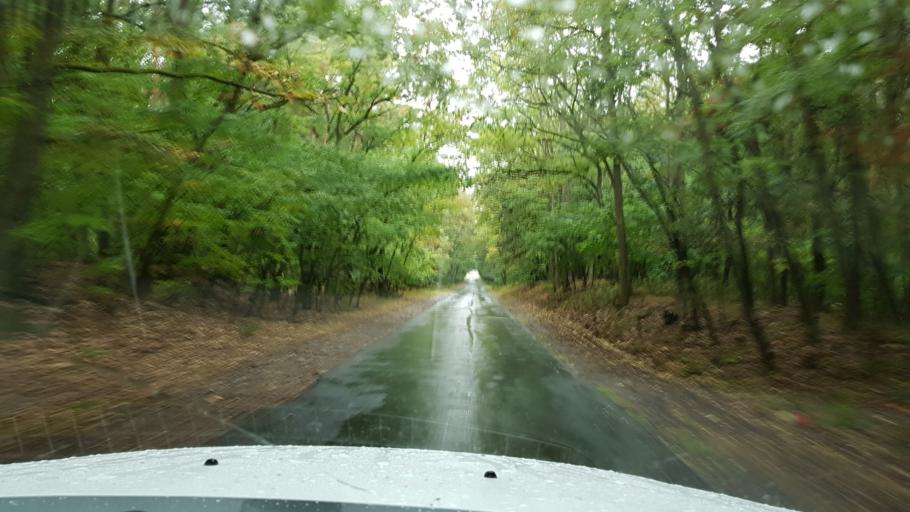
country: DE
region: Brandenburg
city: Meyenburg
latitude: 52.9766
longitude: 14.2249
